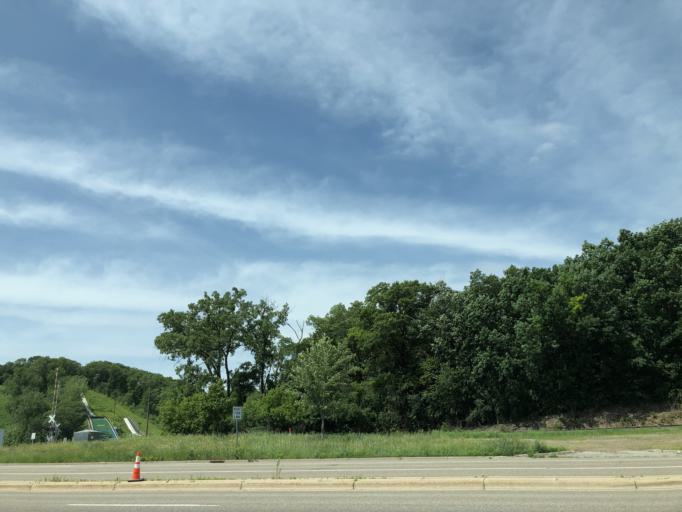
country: US
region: Minnesota
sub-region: Hennepin County
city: Edina
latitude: 44.8545
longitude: -93.3627
